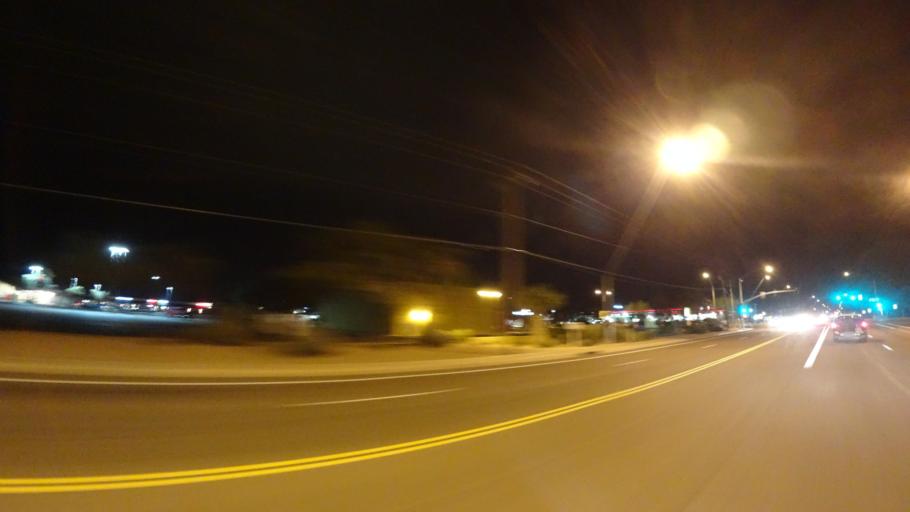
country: US
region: Arizona
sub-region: Maricopa County
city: Gilbert
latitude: 33.4164
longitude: -111.7365
